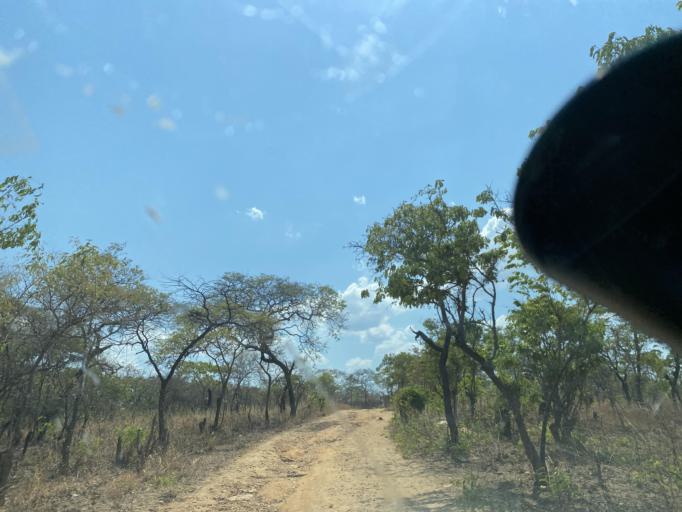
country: ZM
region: Lusaka
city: Chongwe
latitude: -15.0862
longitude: 29.4873
